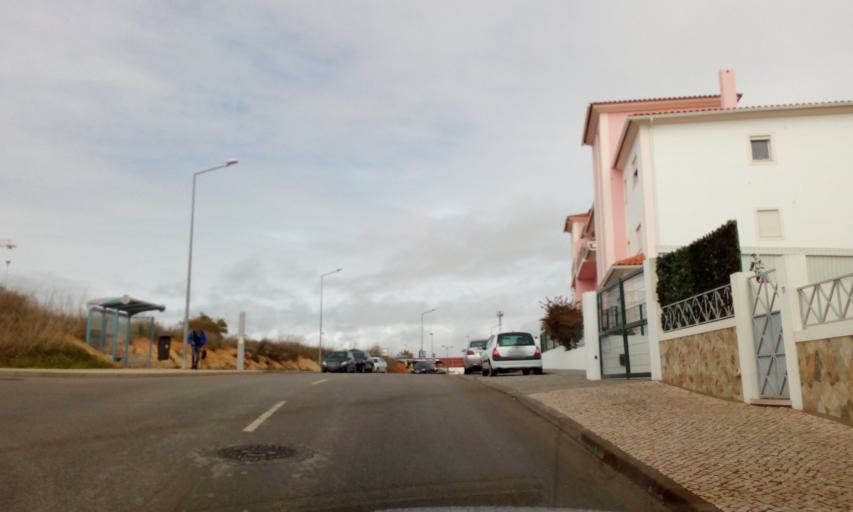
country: PT
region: Faro
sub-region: Albufeira
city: Albufeira
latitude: 37.0931
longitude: -8.2495
